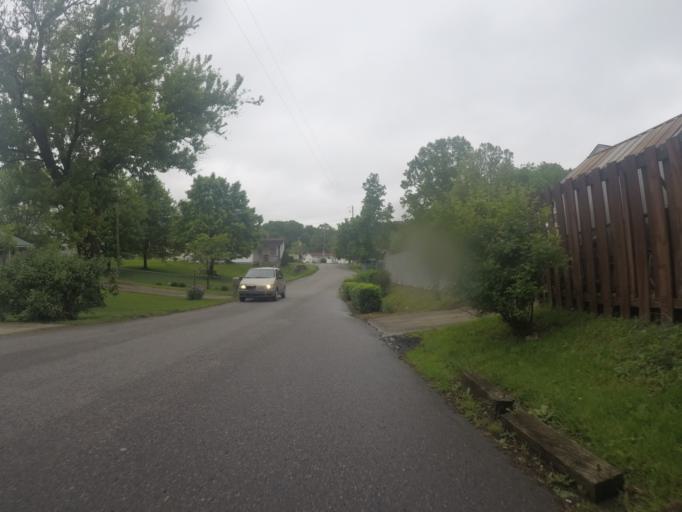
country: US
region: West Virginia
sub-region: Cabell County
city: Barboursville
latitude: 38.4190
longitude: -82.3033
